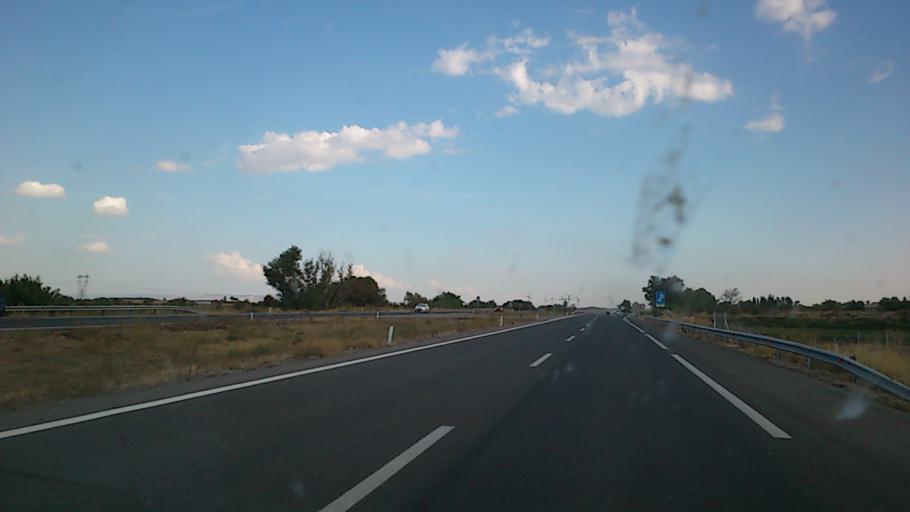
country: ES
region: Aragon
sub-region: Provincia de Zaragoza
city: Frescano
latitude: 41.9128
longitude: -1.4667
